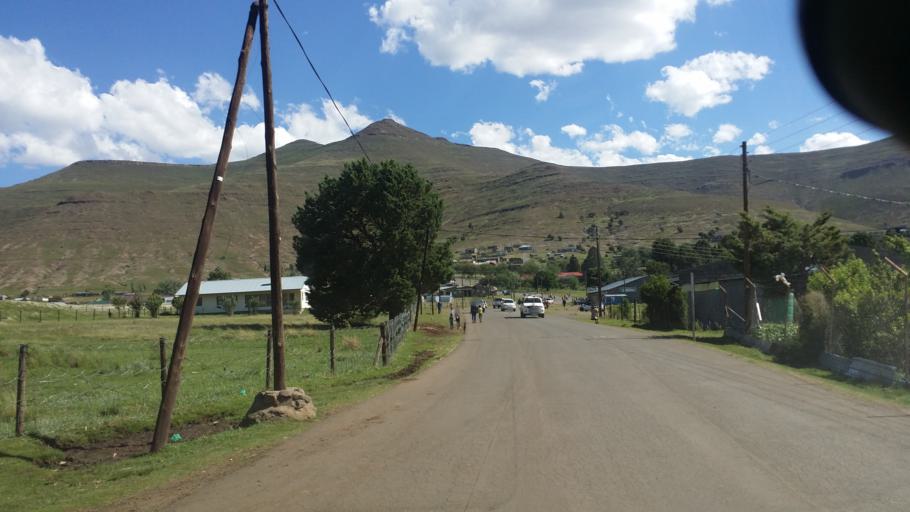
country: LS
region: Mokhotlong
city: Mokhotlong
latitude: -29.2847
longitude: 29.0697
